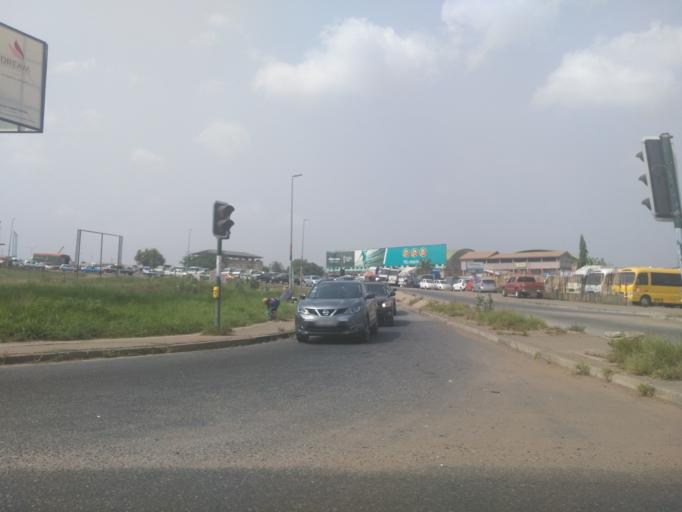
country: GH
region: Greater Accra
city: Dome
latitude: 5.6133
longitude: -0.2288
